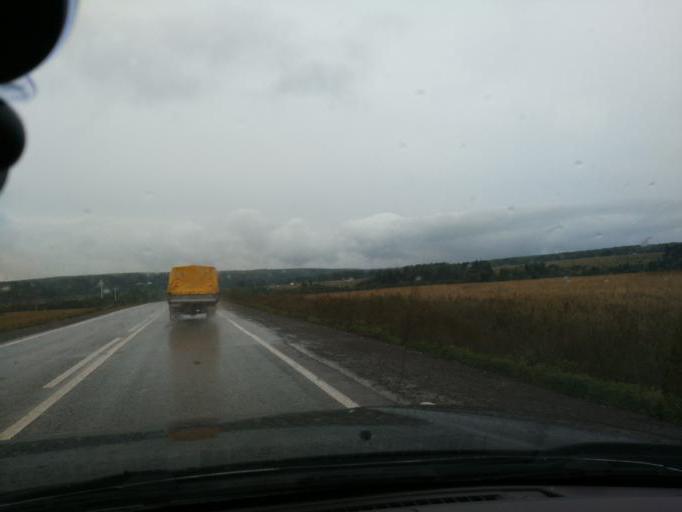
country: RU
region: Perm
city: Yugo-Kamskiy
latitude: 57.7069
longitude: 55.6307
